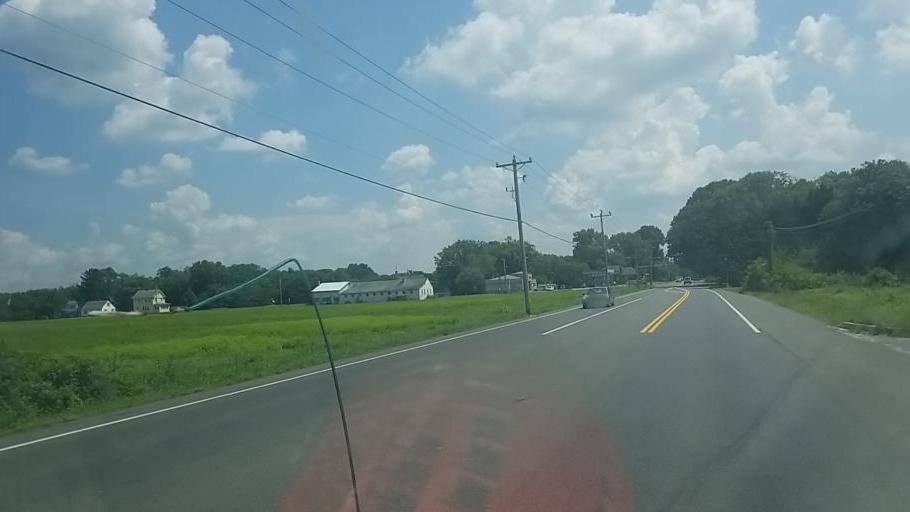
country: US
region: Maryland
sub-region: Wicomico County
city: Salisbury
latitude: 38.3736
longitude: -75.5571
